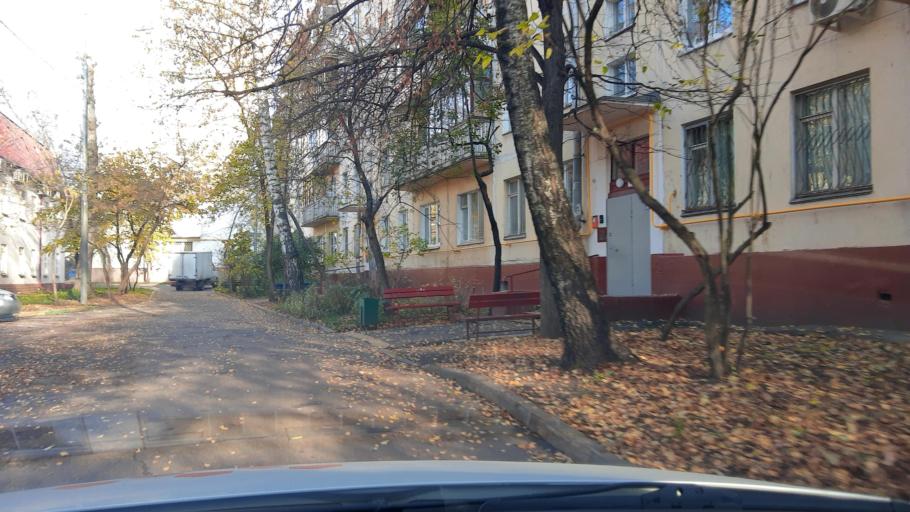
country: RU
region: Moscow
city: Ryazanskiy
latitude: 55.7310
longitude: 37.7687
